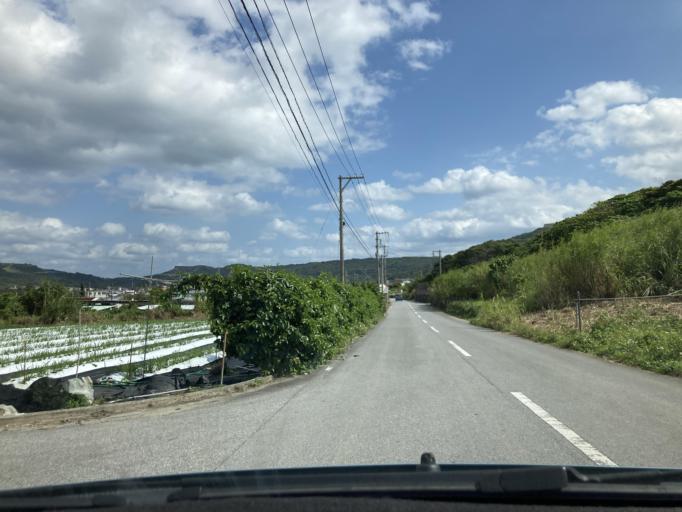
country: JP
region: Okinawa
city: Ginowan
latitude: 26.1693
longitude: 127.7756
